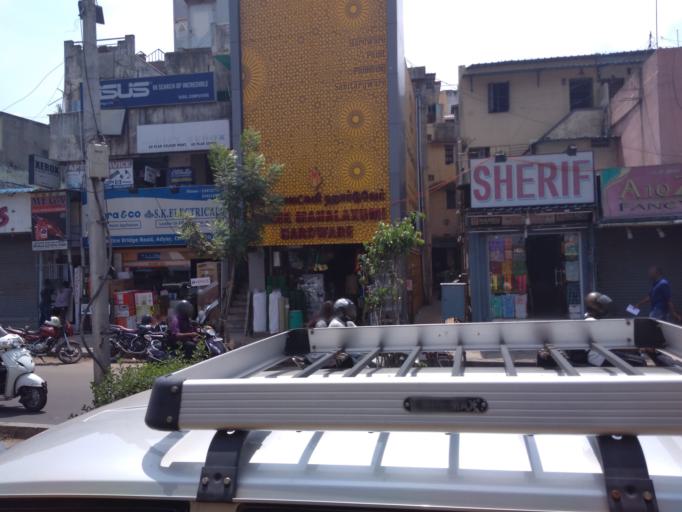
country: IN
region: Tamil Nadu
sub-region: Chennai
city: Gandhi Nagar
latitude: 13.0017
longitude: 80.2565
